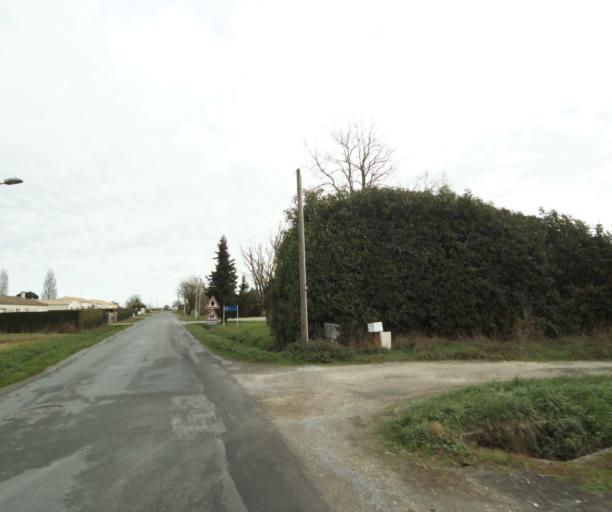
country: FR
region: Poitou-Charentes
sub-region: Departement de la Charente-Maritime
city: Corme-Royal
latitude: 45.7443
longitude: -0.8080
